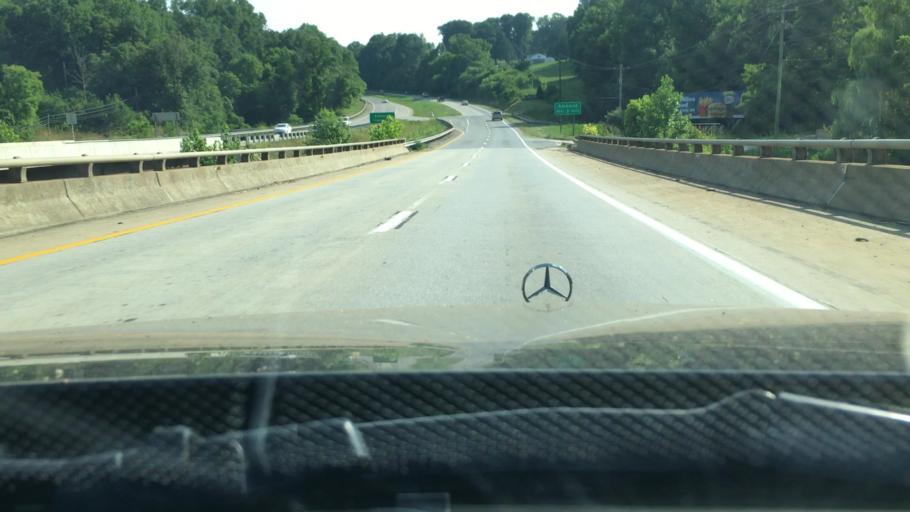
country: US
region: Virginia
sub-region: Amherst County
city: Amherst
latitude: 37.6056
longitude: -79.0260
